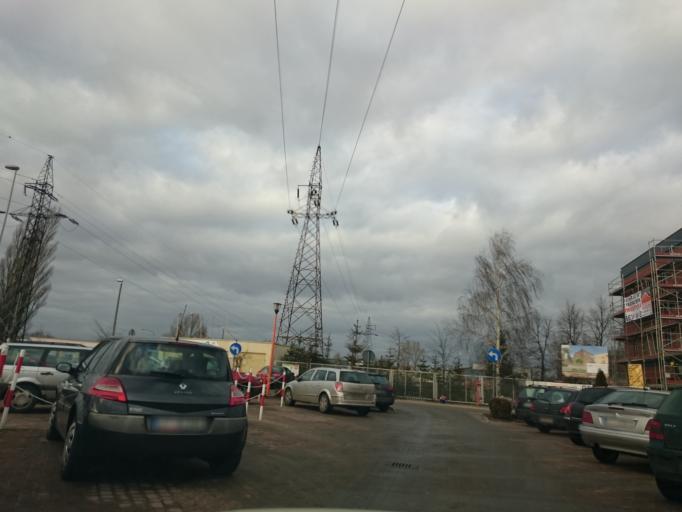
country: PL
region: Kujawsko-Pomorskie
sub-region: Powiat torunski
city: Lysomice
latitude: 53.0374
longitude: 18.6567
